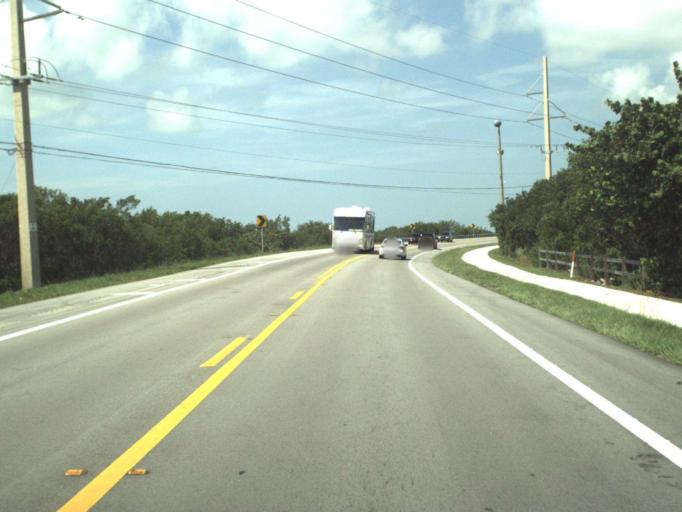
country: US
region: Florida
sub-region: Monroe County
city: Islamorada
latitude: 24.8370
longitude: -80.7612
